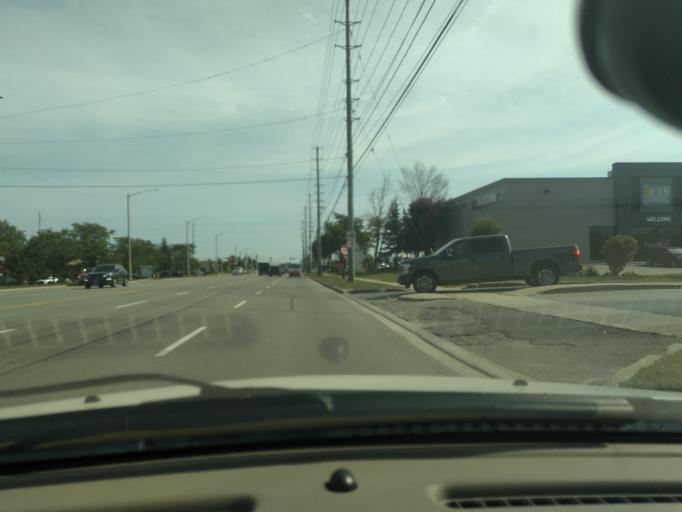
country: CA
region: Ontario
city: Innisfil
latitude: 44.3330
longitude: -79.6951
